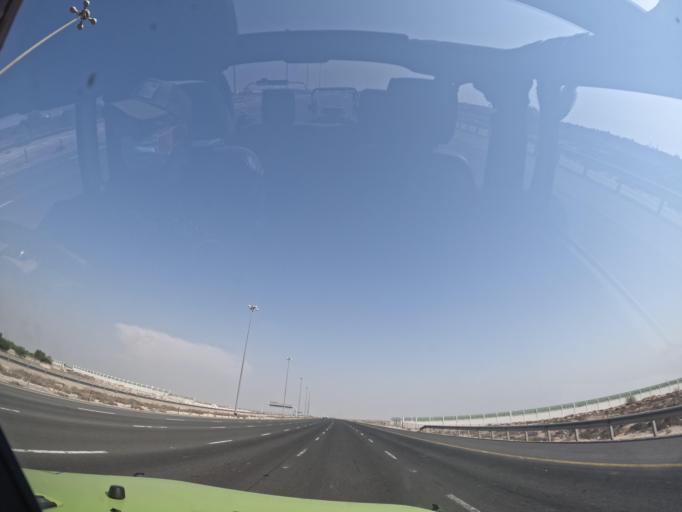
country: AE
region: Abu Dhabi
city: Abu Dhabi
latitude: 24.6895
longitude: 54.7865
